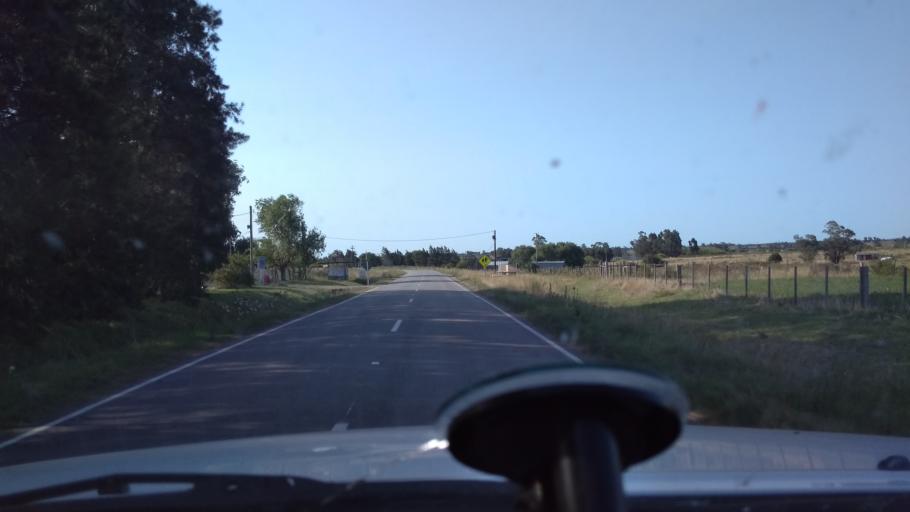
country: UY
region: Canelones
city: Sauce
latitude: -34.5997
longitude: -56.1338
